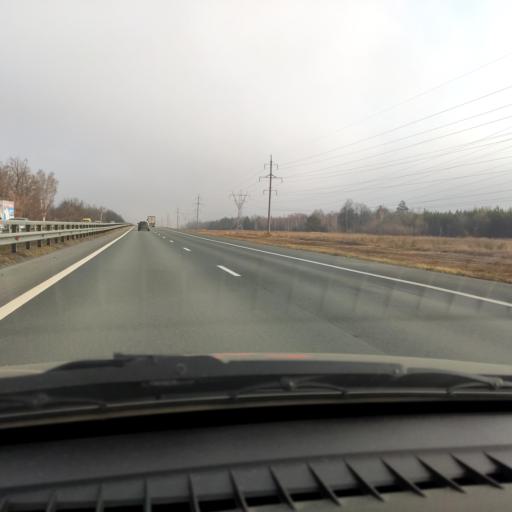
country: RU
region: Samara
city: Pribrezhnyy
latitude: 53.5174
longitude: 49.7919
